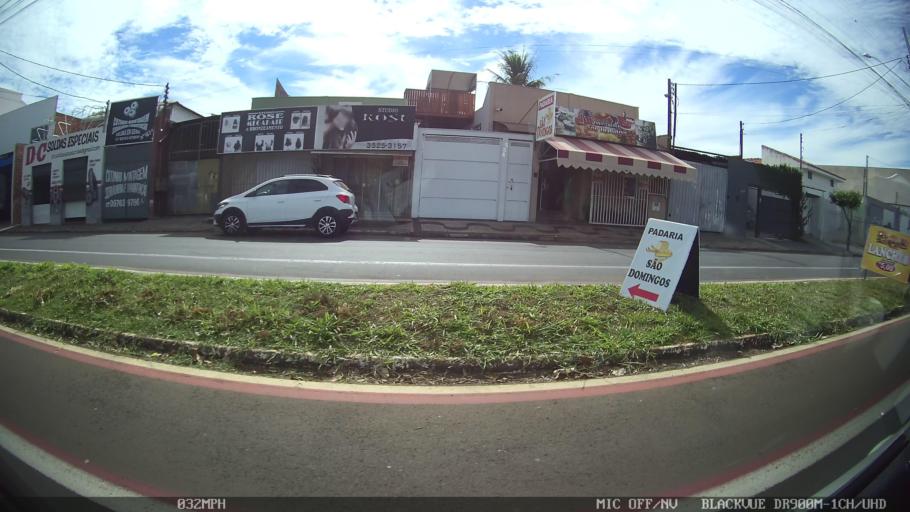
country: BR
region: Sao Paulo
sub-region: Catanduva
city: Catanduva
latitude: -21.1419
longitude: -48.9520
